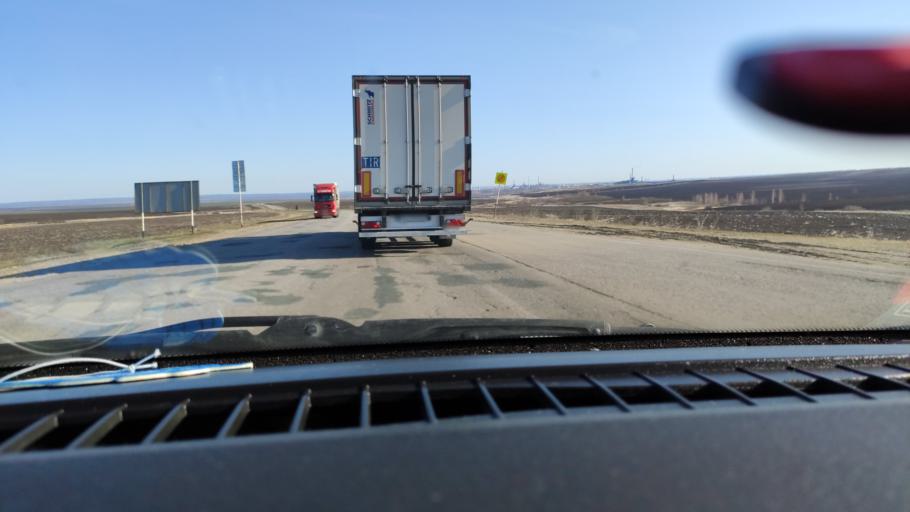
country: RU
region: Samara
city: Syzran'
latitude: 53.0040
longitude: 48.3309
